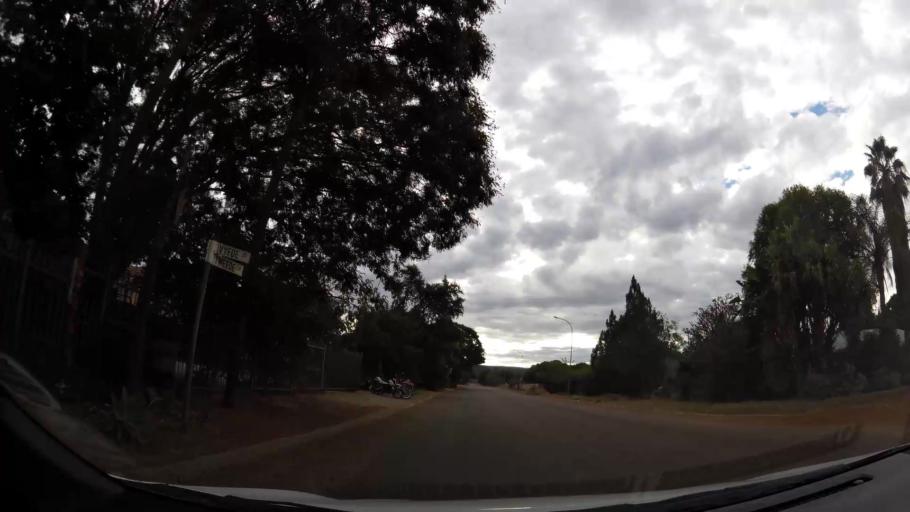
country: ZA
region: Limpopo
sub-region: Waterberg District Municipality
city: Modimolle
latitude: -24.5226
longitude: 28.7070
